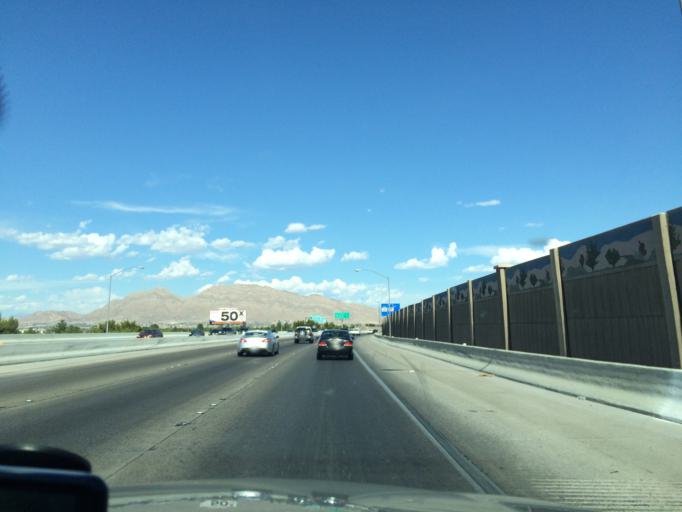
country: US
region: Nevada
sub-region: Clark County
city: Las Vegas
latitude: 36.1675
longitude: -115.1039
